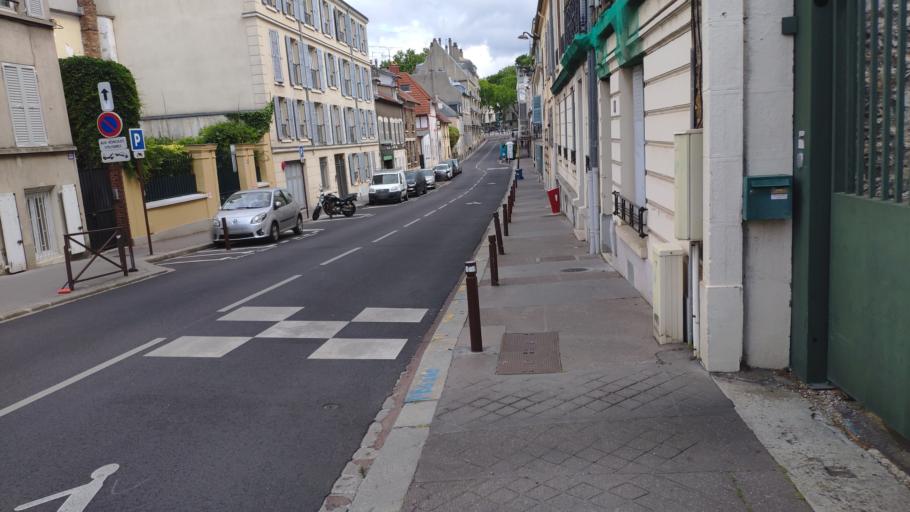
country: FR
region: Ile-de-France
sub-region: Departement des Yvelines
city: Versailles
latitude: 48.7981
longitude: 2.1376
